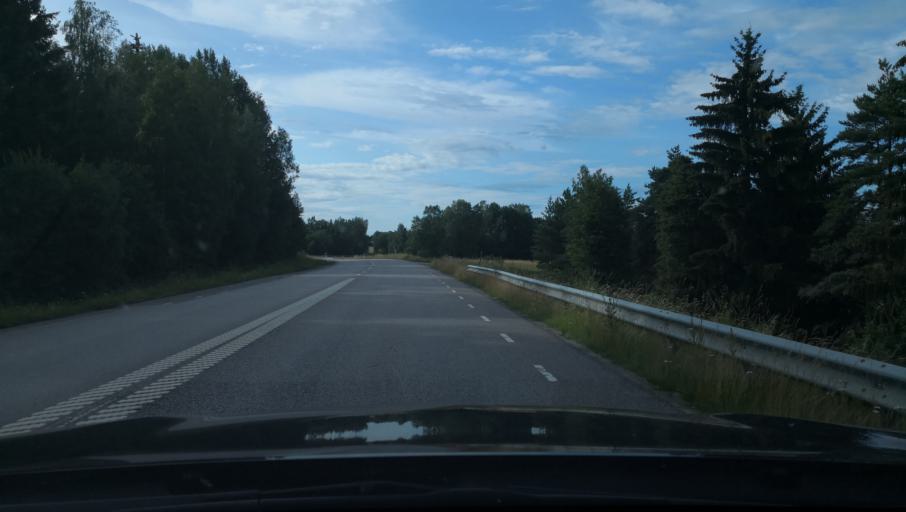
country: SE
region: Uppsala
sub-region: Habo Kommun
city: Balsta
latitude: 59.6059
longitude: 17.5055
